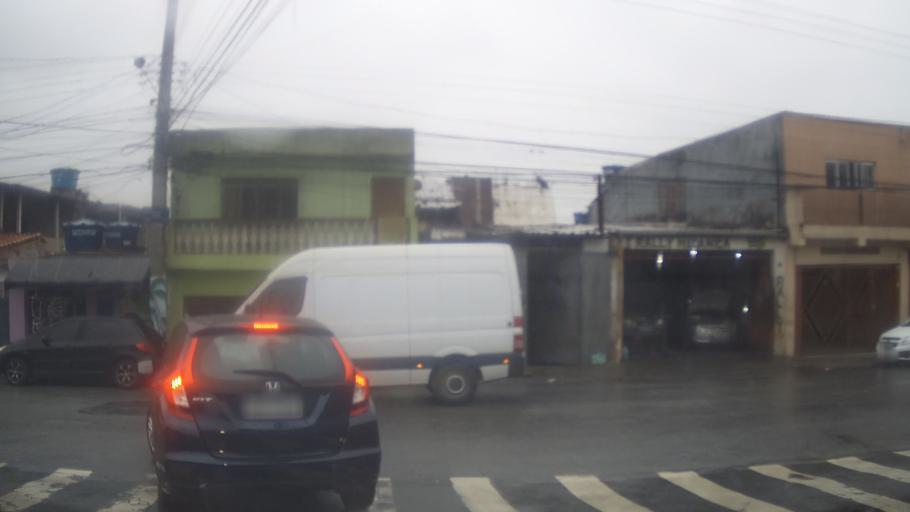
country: BR
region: Sao Paulo
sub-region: Guarulhos
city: Guarulhos
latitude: -23.4377
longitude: -46.5182
